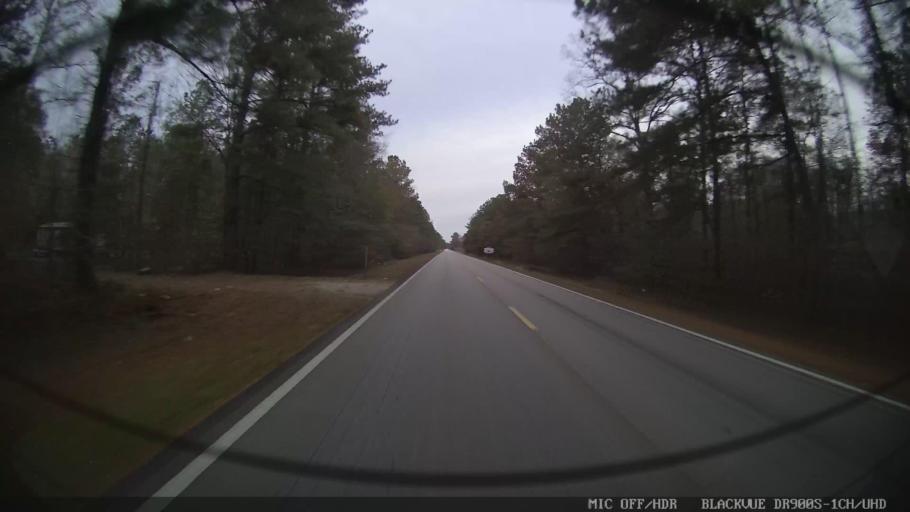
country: US
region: Mississippi
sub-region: Clarke County
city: Stonewall
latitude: 32.0320
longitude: -88.8689
